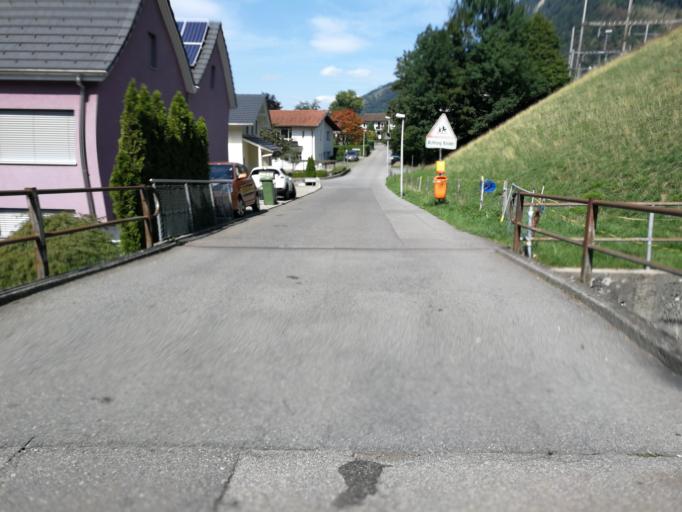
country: CH
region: Schwyz
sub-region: Bezirk Schwyz
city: Goldau
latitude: 47.0506
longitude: 8.5477
